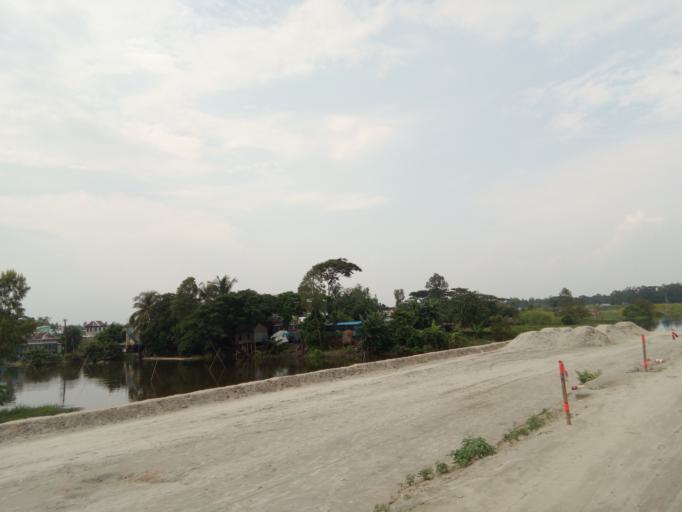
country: BD
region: Dhaka
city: Dohar
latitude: 23.5794
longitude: 90.3054
